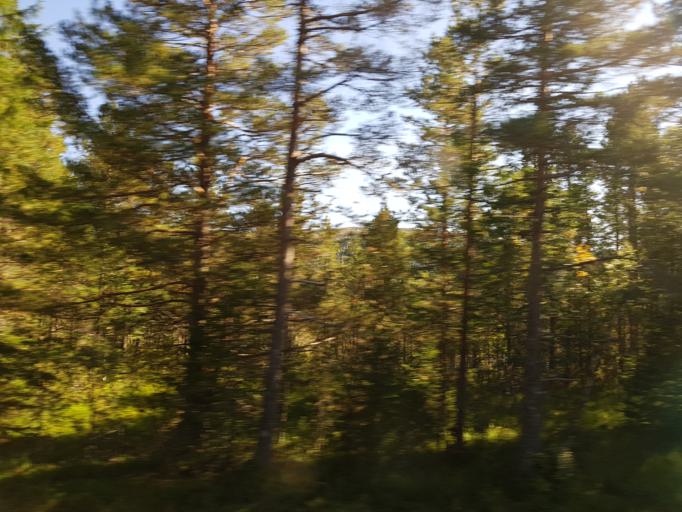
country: NO
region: Sor-Trondelag
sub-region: Afjord
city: A i Afjord
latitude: 63.7852
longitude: 10.2279
